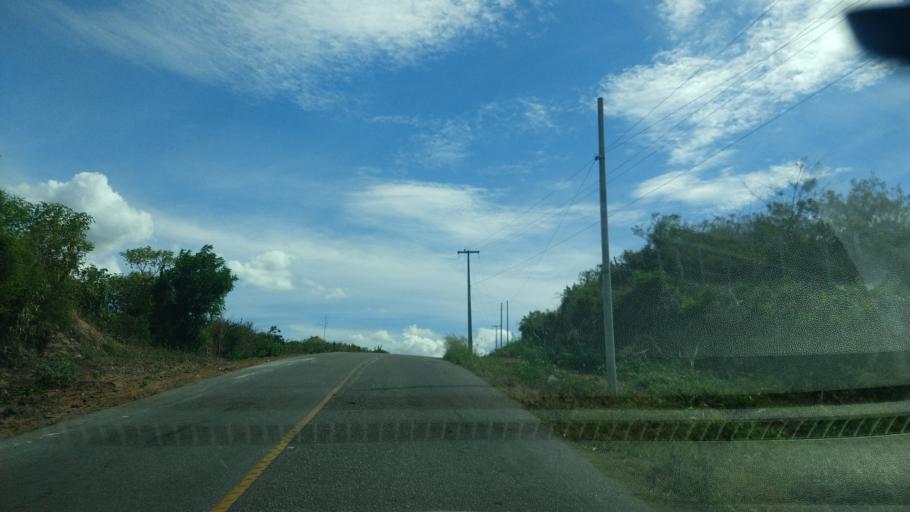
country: BR
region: Rio Grande do Norte
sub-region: Sao Jose Do Campestre
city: Sao Jose do Campestre
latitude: -6.4196
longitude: -35.7185
